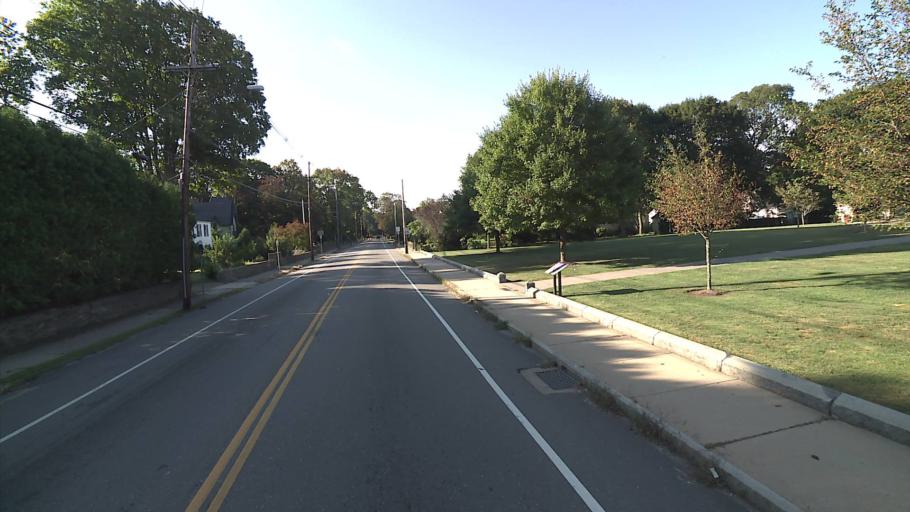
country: US
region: Connecticut
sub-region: New London County
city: Norwich
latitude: 41.5349
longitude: -72.0833
